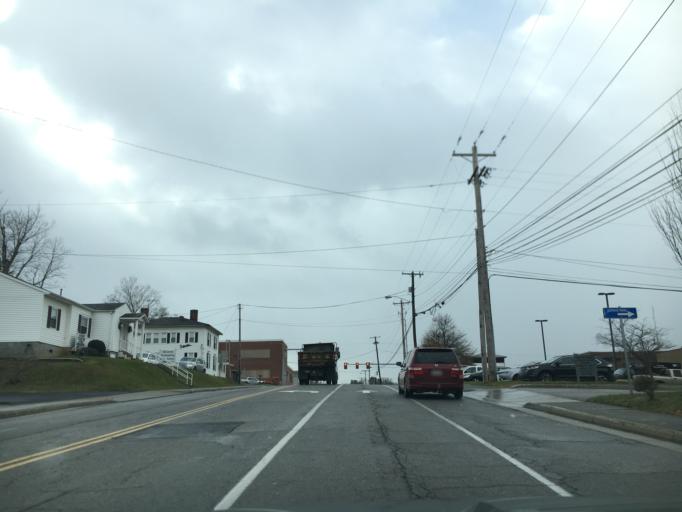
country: US
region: Virginia
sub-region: Montgomery County
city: Christiansburg
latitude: 37.1298
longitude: -80.4068
